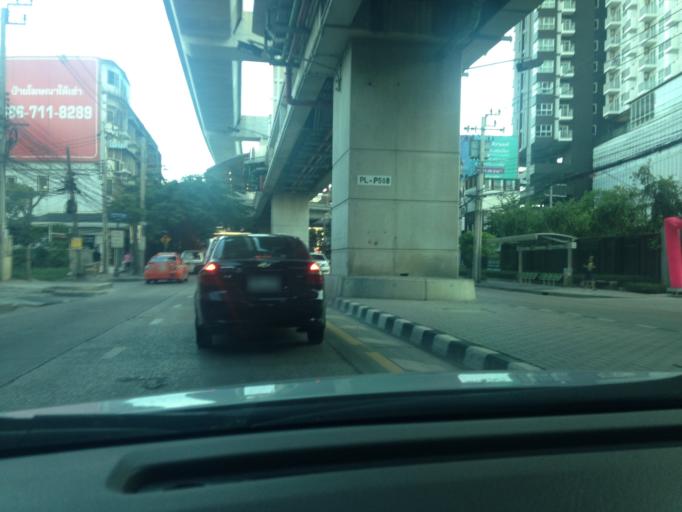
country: TH
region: Bangkok
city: Bang Sue
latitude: 13.8295
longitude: 100.5272
